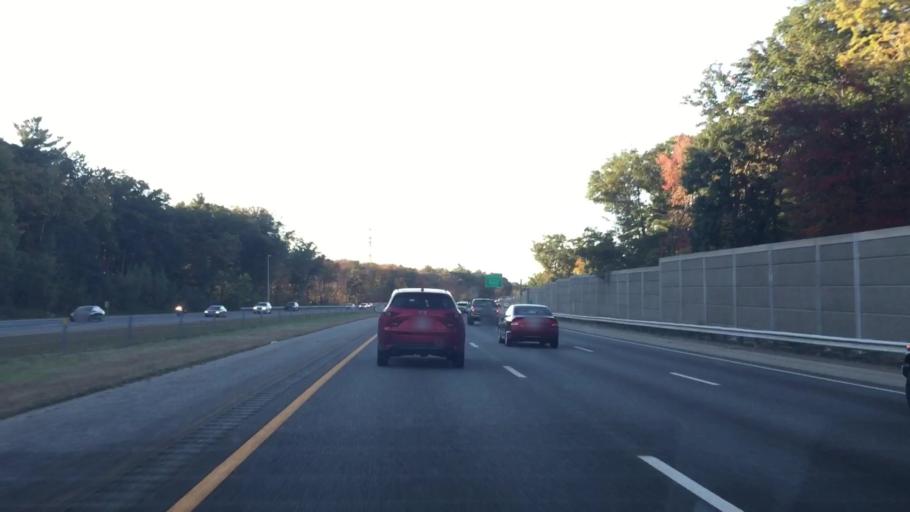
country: US
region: Massachusetts
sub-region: Middlesex County
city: Billerica
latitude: 42.5267
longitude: -71.2692
